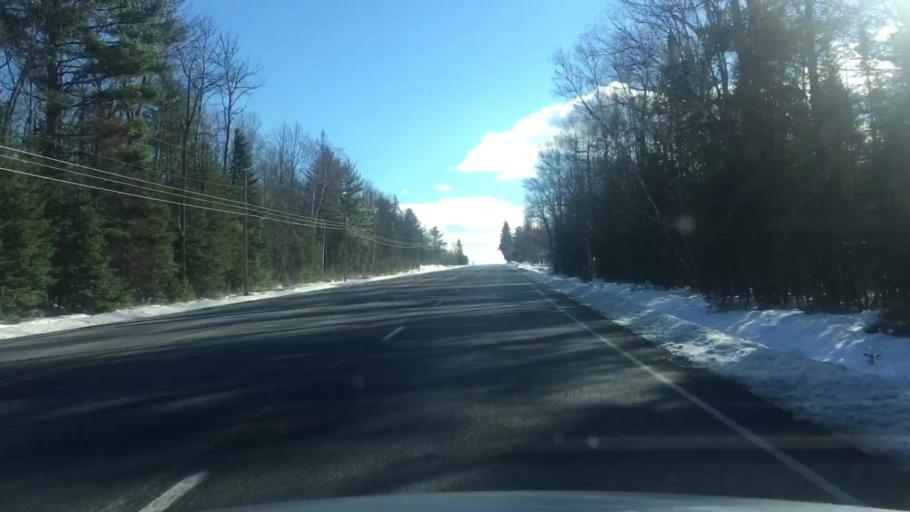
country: US
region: Maine
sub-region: Somerset County
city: Madison
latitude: 44.8976
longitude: -69.8099
